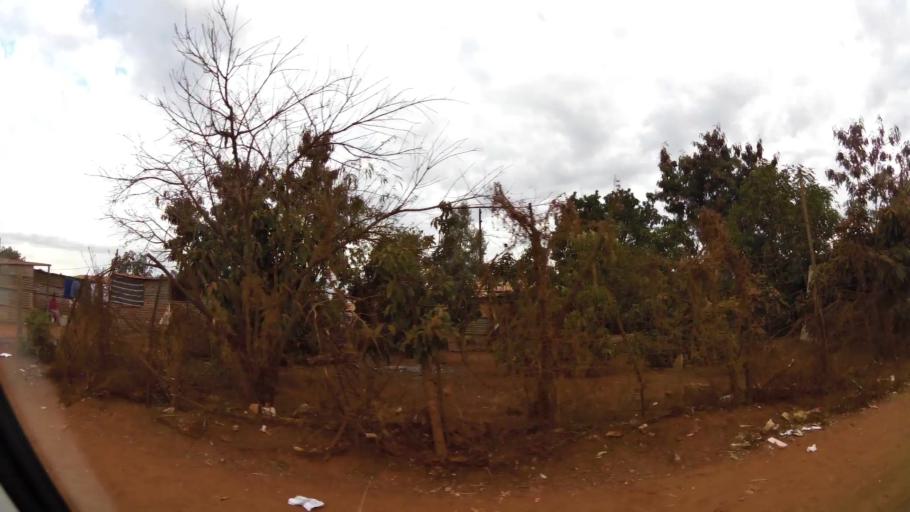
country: ZA
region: Limpopo
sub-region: Waterberg District Municipality
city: Modimolle
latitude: -24.5264
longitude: 28.7207
